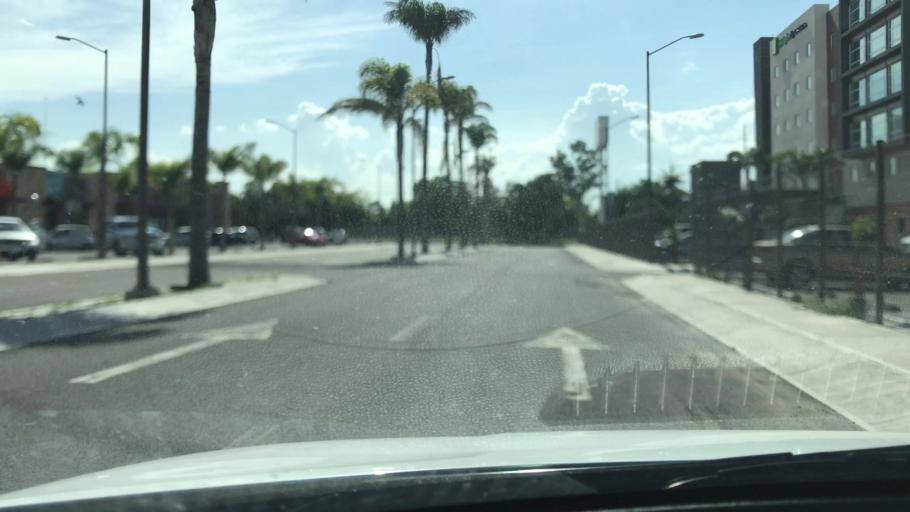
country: MX
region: Guanajuato
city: Celaya
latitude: 20.5164
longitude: -100.7787
